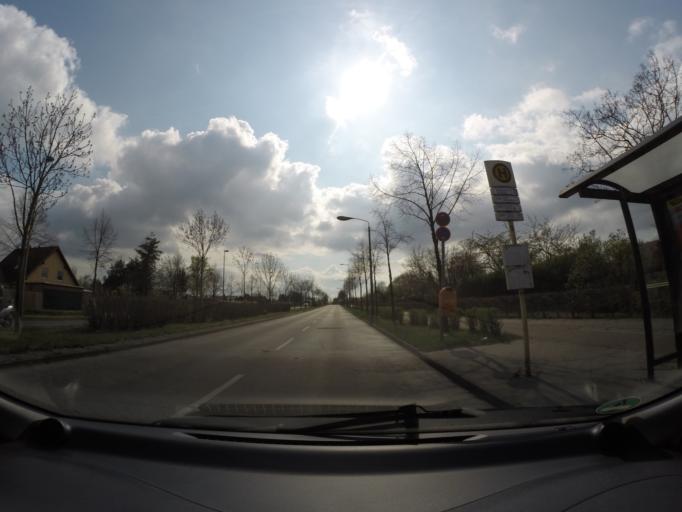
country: DE
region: Berlin
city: Marzahn
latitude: 52.5353
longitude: 13.5844
